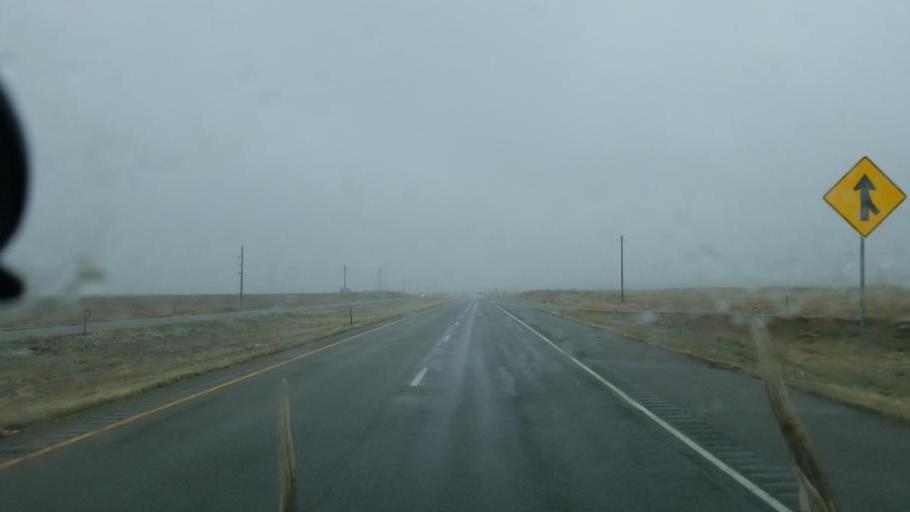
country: US
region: Colorado
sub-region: Pueblo County
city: Colorado City
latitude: 37.8622
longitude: -104.8286
